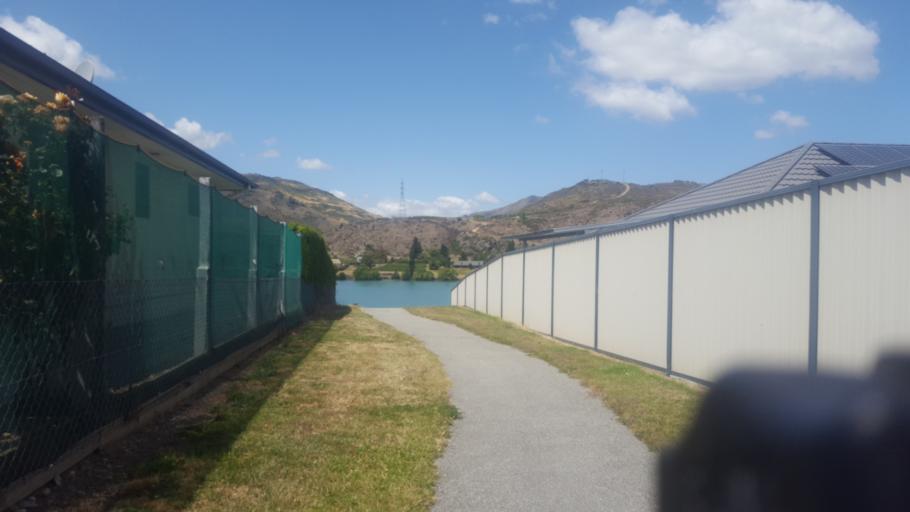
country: NZ
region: Otago
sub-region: Queenstown-Lakes District
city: Wanaka
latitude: -45.0510
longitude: 169.1976
